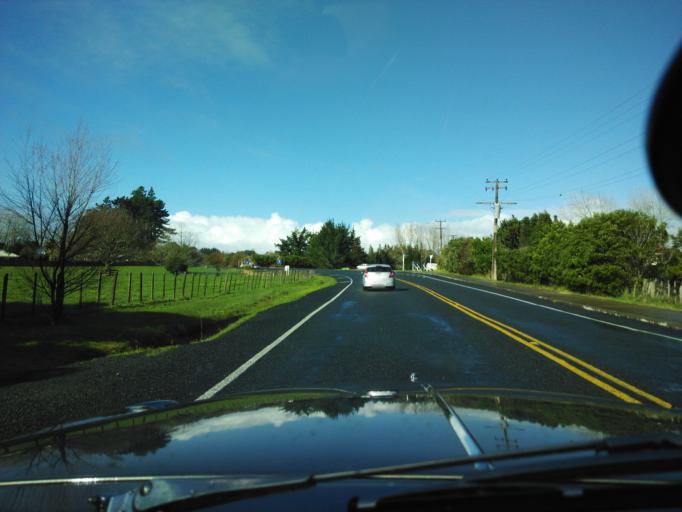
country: NZ
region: Auckland
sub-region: Auckland
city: Parakai
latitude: -36.6393
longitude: 174.5588
